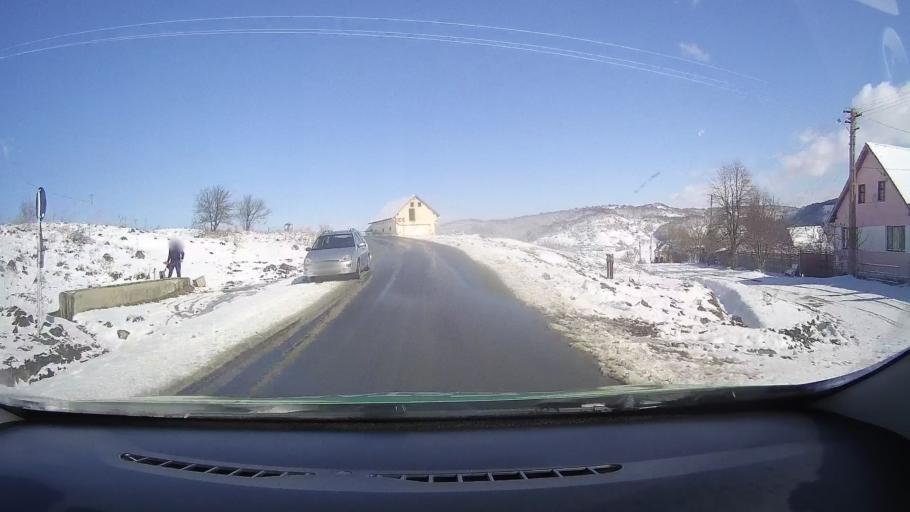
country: RO
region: Sibiu
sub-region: Comuna Rosia
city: Rosia
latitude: 45.7974
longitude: 24.3862
